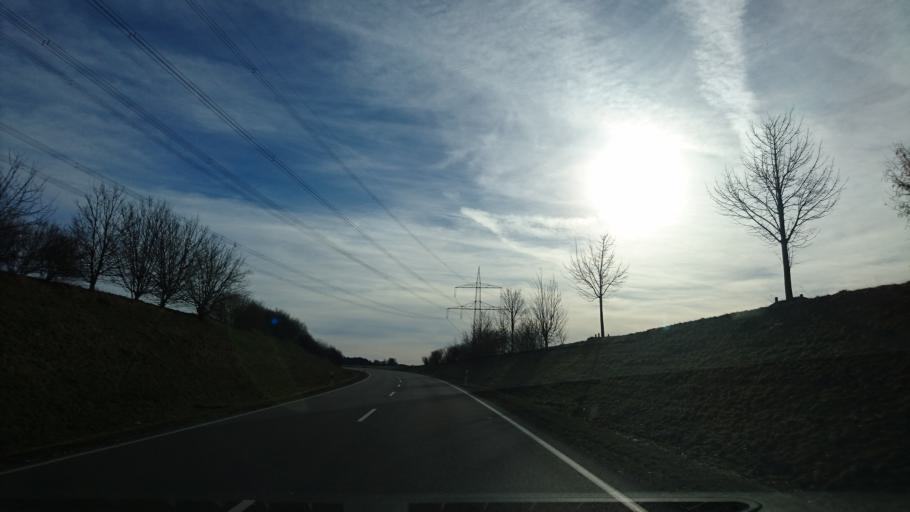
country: DE
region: Bavaria
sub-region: Swabia
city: Laugna
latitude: 48.5311
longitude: 10.7549
